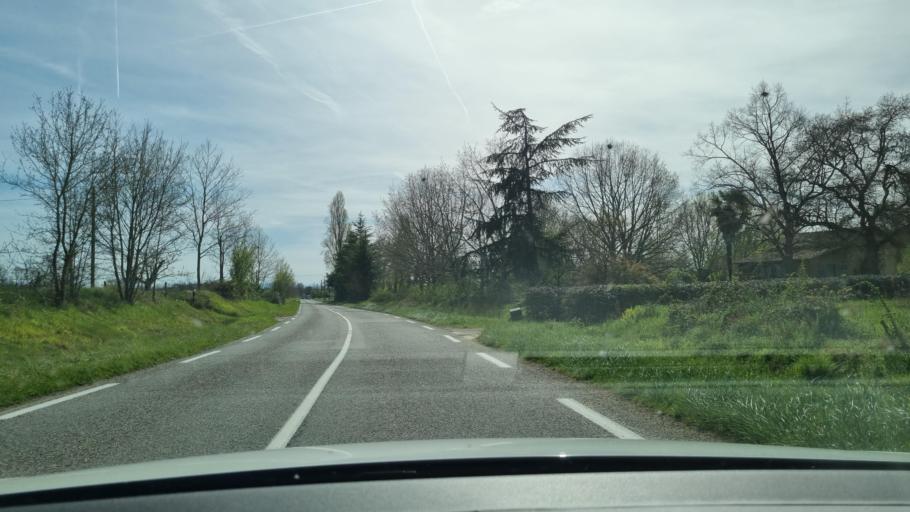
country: FR
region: Midi-Pyrenees
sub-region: Departement du Gers
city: Lombez
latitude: 43.4130
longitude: 0.8052
